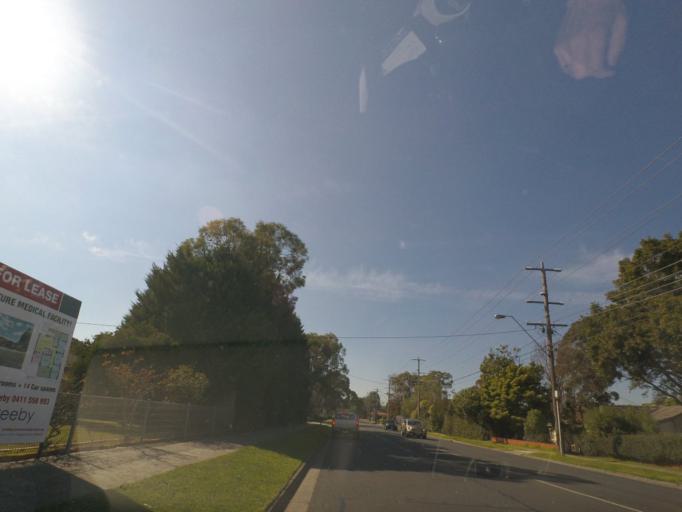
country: AU
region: Victoria
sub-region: Maroondah
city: Ringwood East
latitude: -37.8053
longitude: 145.2279
